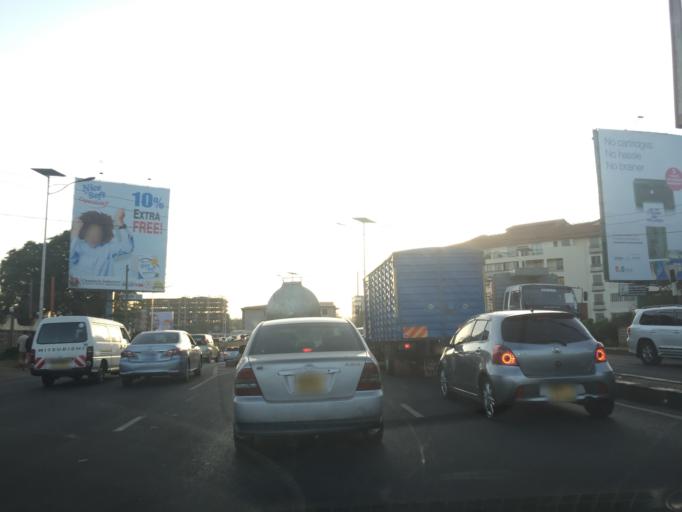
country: KE
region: Nairobi Area
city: Nairobi
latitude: -1.2702
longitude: 36.8156
